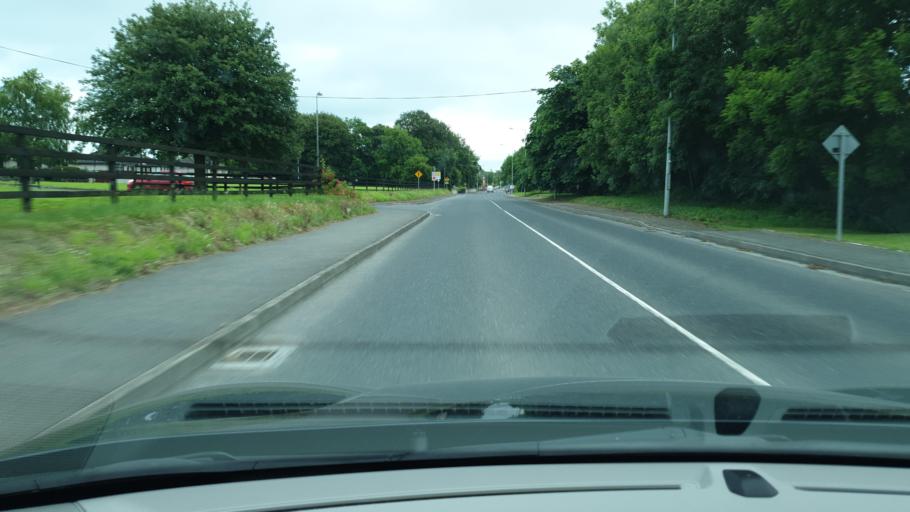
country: IE
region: Leinster
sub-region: An Mhi
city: Dunshaughlin
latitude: 53.4711
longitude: -6.5391
